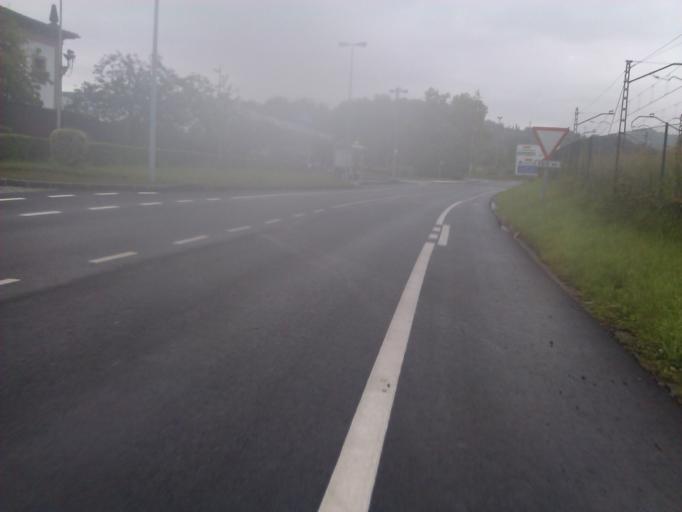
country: ES
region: Basque Country
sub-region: Provincia de Guipuzcoa
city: San Sebastian
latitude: 43.3029
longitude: -1.9584
